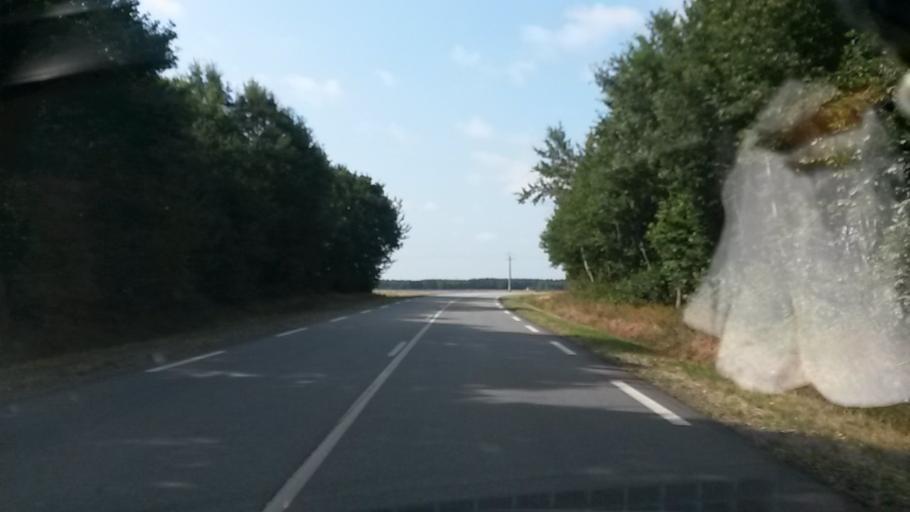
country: FR
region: Haute-Normandie
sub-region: Departement de l'Eure
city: Damville
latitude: 48.8539
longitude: 1.0608
